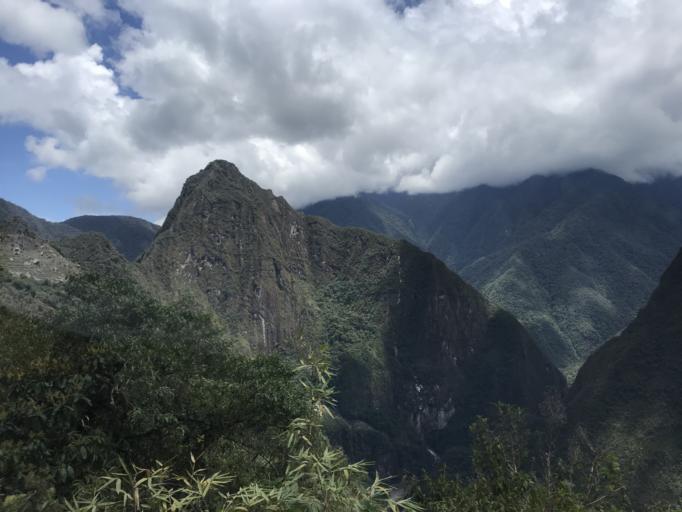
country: PE
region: Cusco
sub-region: Provincia de La Convencion
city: Santa Teresa
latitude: -13.1675
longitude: -72.5395
